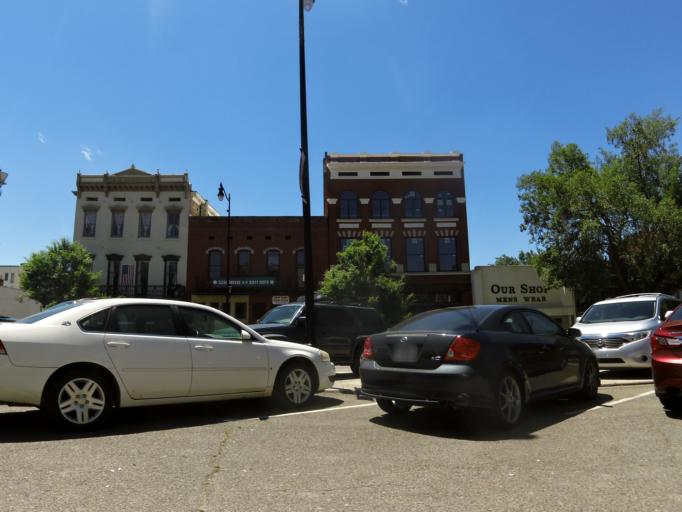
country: US
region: Georgia
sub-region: Richmond County
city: Augusta
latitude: 33.4769
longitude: -81.9700
